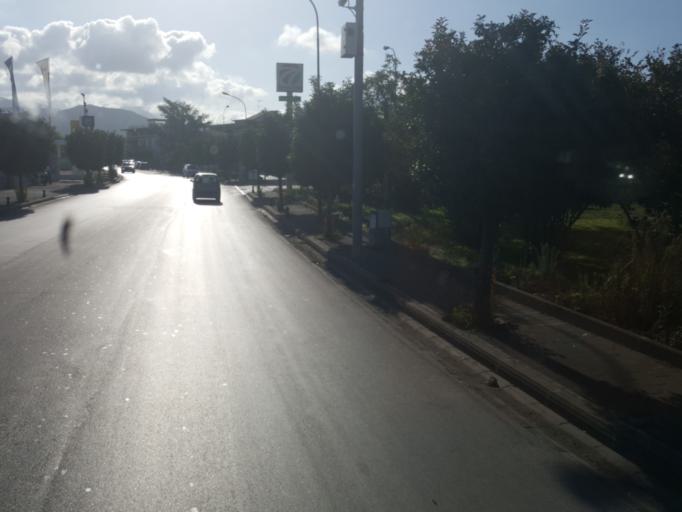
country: IT
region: Campania
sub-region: Provincia di Napoli
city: Nola
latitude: 40.9176
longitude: 14.5187
